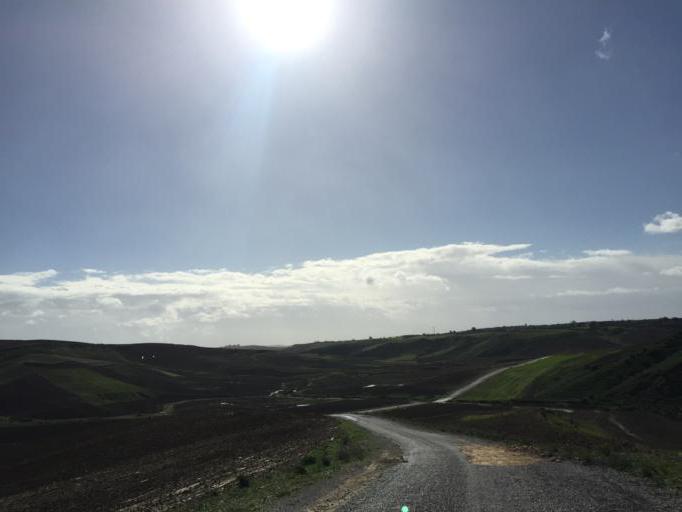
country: TN
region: Nabul
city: El Mida
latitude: 36.8621
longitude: 10.8606
